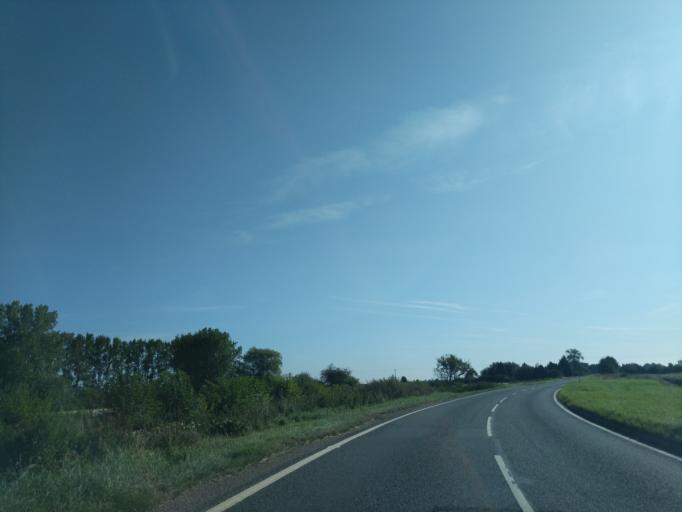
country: GB
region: England
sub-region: Lincolnshire
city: Bourne
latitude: 52.7709
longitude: -0.3578
